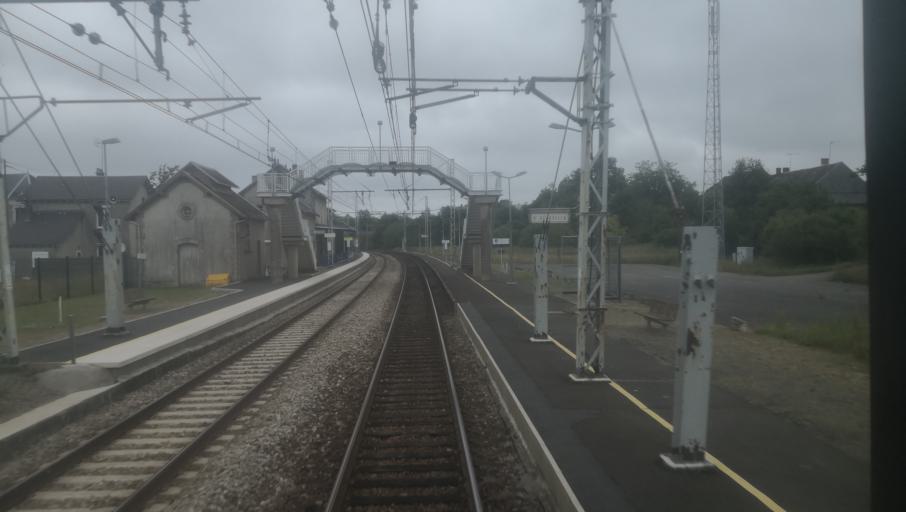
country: FR
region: Centre
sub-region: Departement de l'Indre
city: Chantome
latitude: 46.3854
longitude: 1.5464
